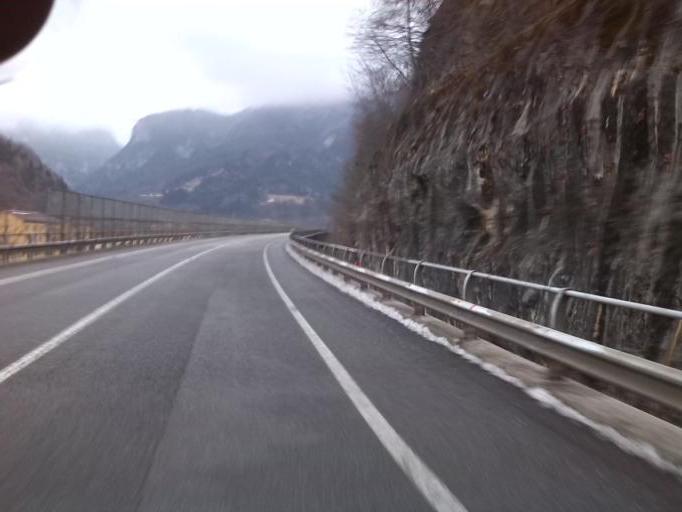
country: IT
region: Friuli Venezia Giulia
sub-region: Provincia di Udine
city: Pontebba
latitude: 46.4958
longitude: 13.3013
